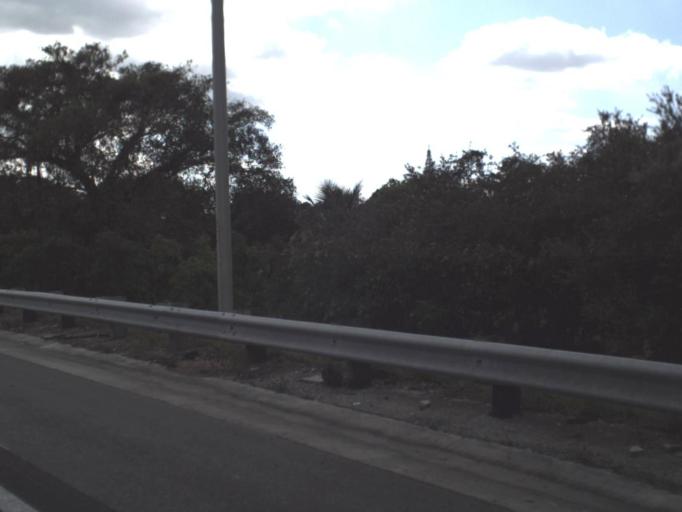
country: US
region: Florida
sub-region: Broward County
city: Pembroke Pines
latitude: 26.0169
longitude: -80.2129
